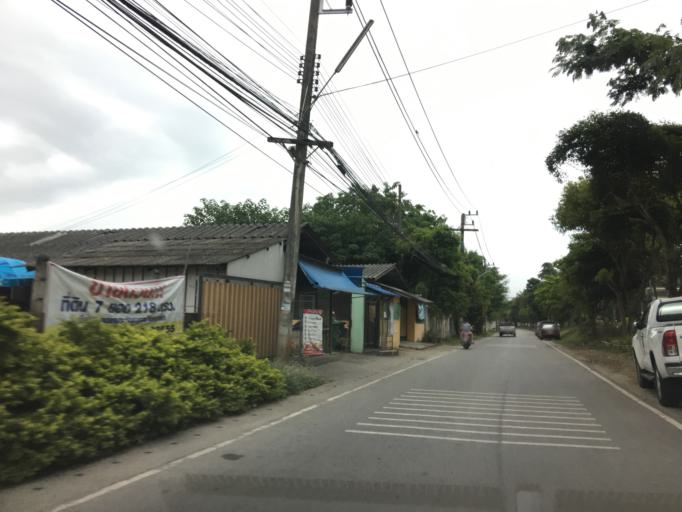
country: TH
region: Chiang Mai
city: Chiang Mai
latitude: 18.8137
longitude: 98.9691
